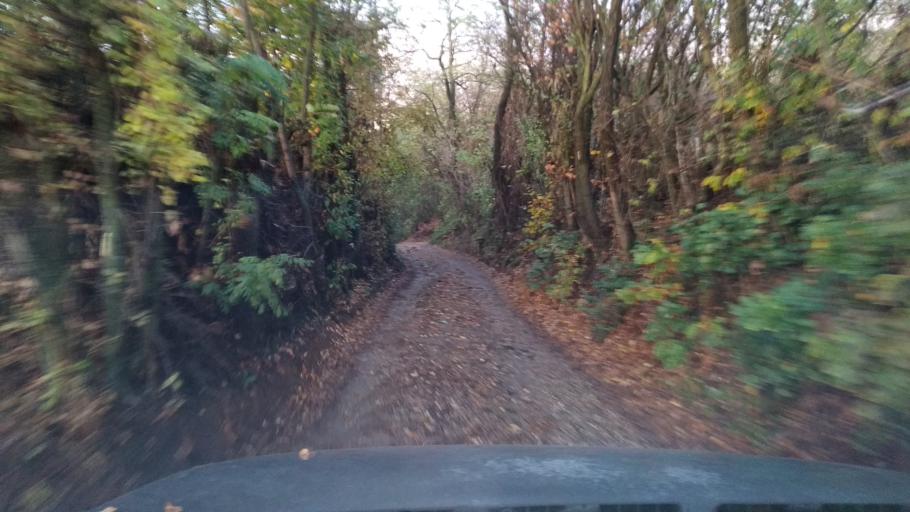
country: HU
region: Pest
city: Nagykovacsi
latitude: 47.6630
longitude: 18.9995
